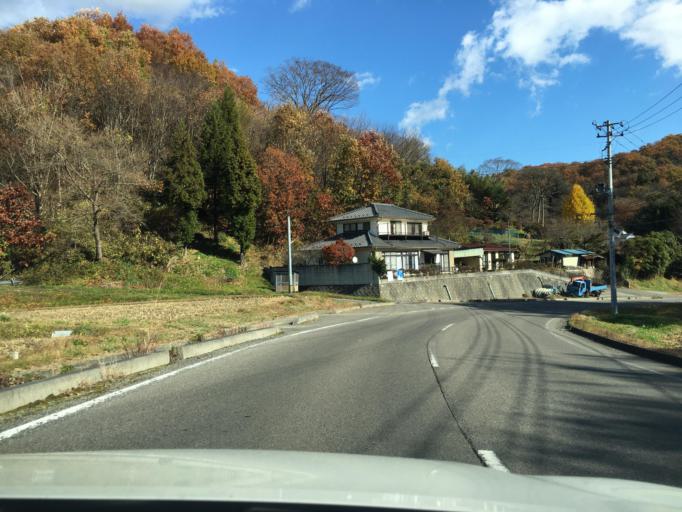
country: JP
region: Fukushima
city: Miharu
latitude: 37.4475
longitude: 140.4667
